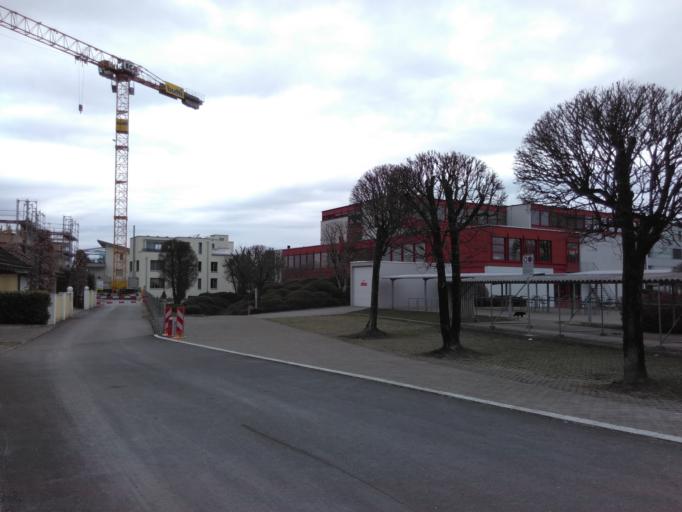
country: CH
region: Schwyz
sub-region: Bezirk March
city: Schubelbach
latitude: 47.1805
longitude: 8.9015
